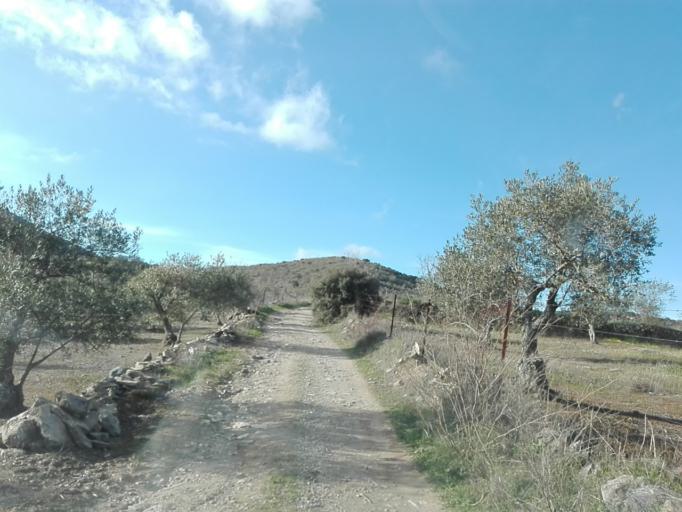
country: ES
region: Extremadura
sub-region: Provincia de Badajoz
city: Trasierra
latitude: 38.2004
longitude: -5.9951
